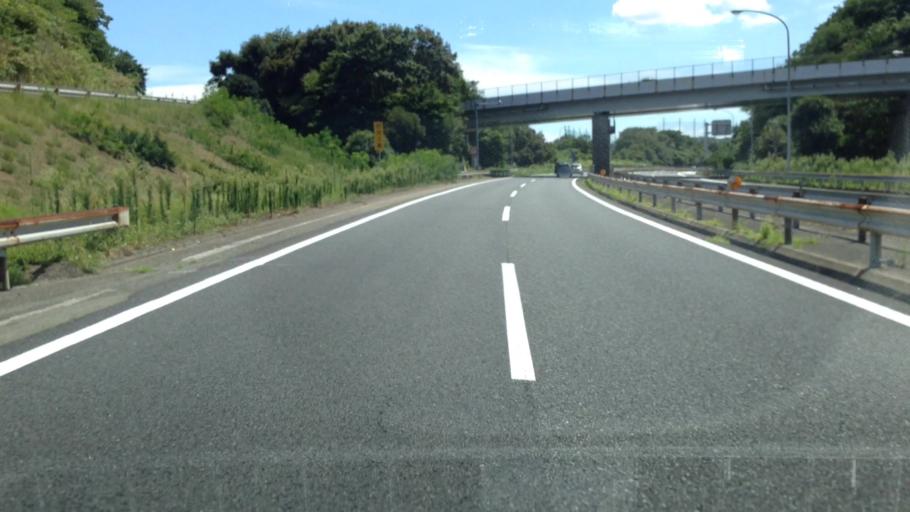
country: JP
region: Kanagawa
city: Yokosuka
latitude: 35.2779
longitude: 139.6335
